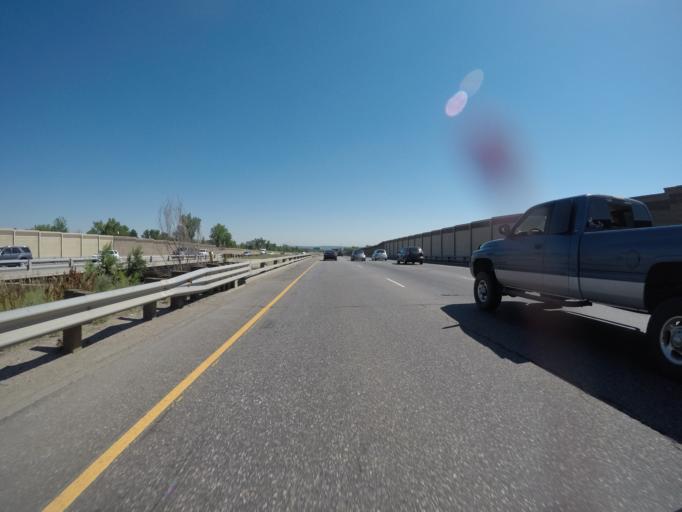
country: US
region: Colorado
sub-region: Jefferson County
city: Applewood
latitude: 39.7471
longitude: -105.1510
